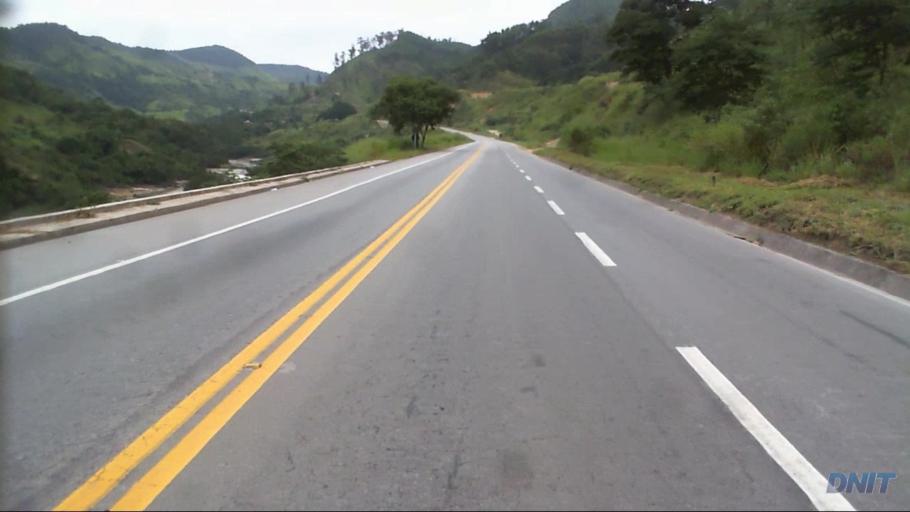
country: BR
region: Minas Gerais
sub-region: Timoteo
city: Timoteo
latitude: -19.6219
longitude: -42.8035
